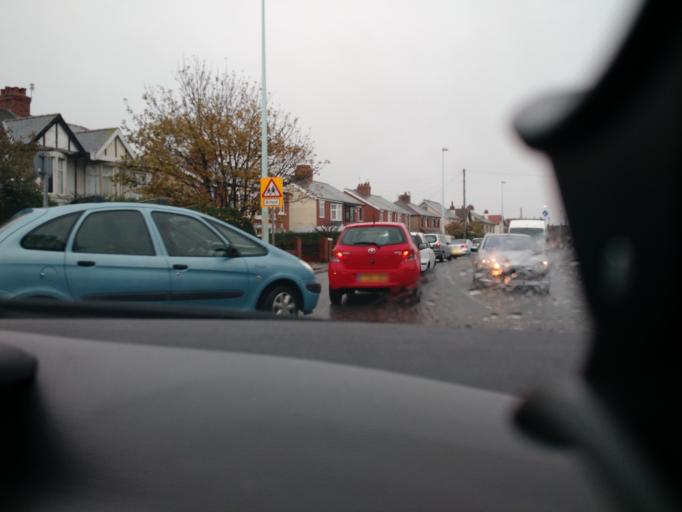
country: GB
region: England
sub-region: Blackpool
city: Blackpool
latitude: 53.8435
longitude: -3.0327
